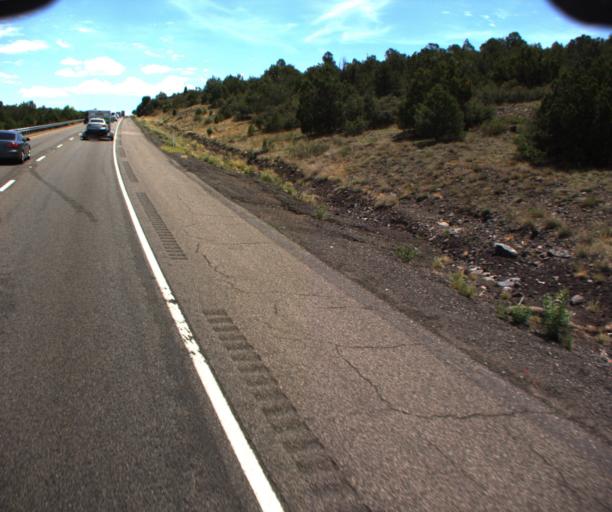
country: US
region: Arizona
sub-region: Yavapai County
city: Village of Oak Creek (Big Park)
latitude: 34.7733
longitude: -111.6359
